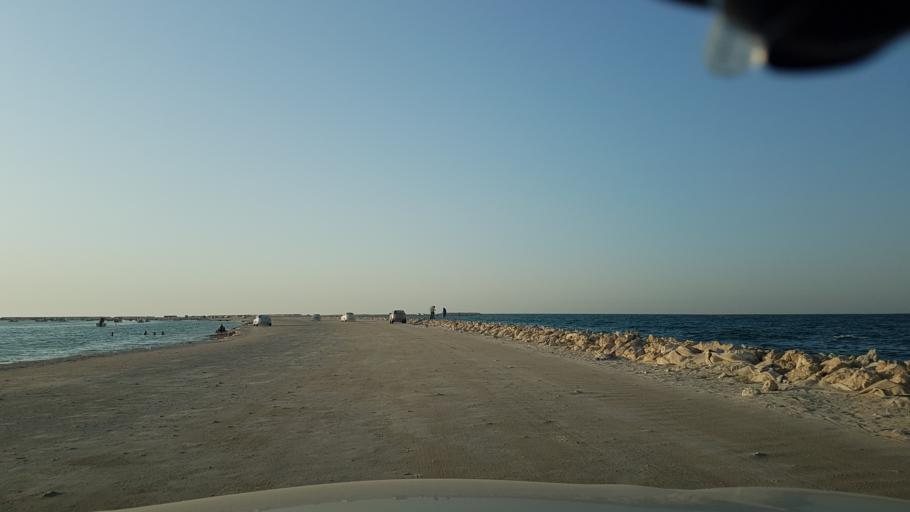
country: BH
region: Manama
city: Jidd Hafs
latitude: 26.2504
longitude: 50.5025
